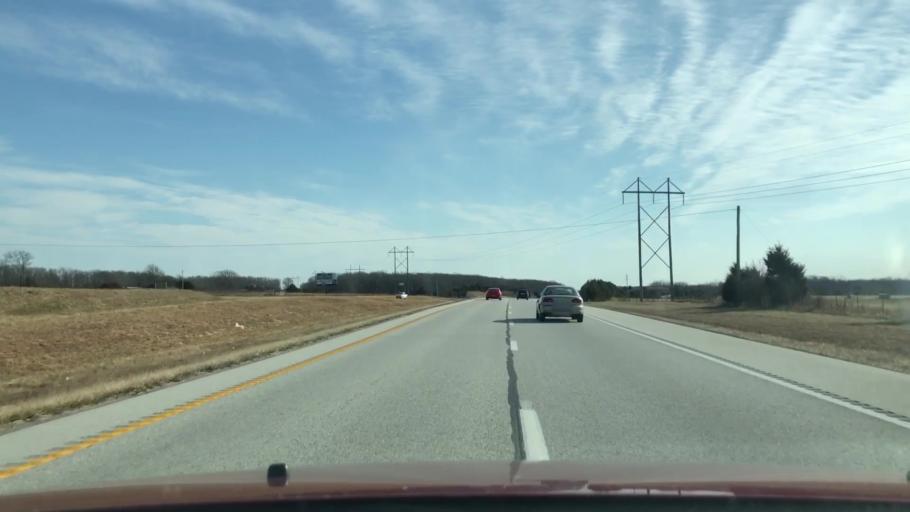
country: US
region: Missouri
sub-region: Webster County
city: Seymour
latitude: 37.1175
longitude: -92.6817
